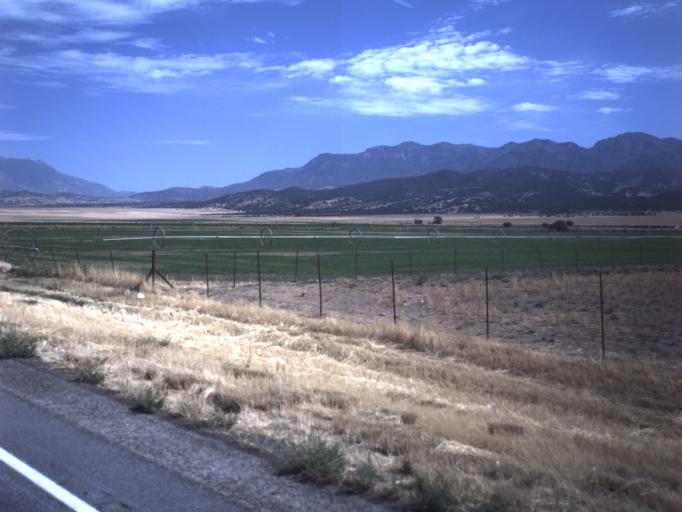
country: US
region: Utah
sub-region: Juab County
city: Nephi
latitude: 39.5659
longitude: -111.8619
